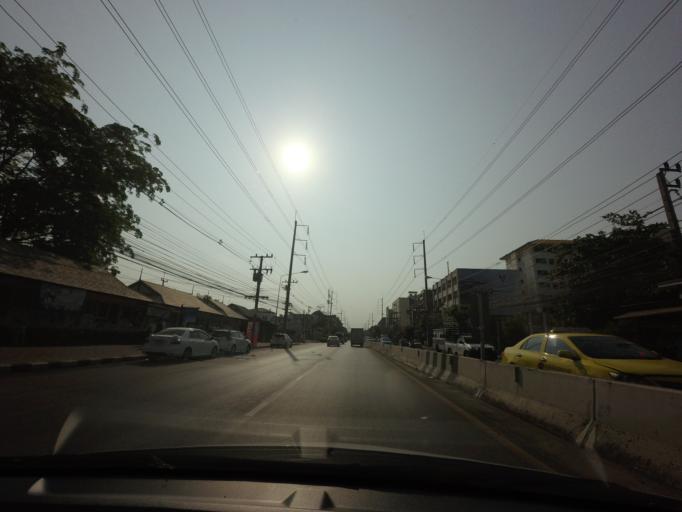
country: TH
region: Nakhon Pathom
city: Salaya
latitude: 13.8015
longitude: 100.3161
